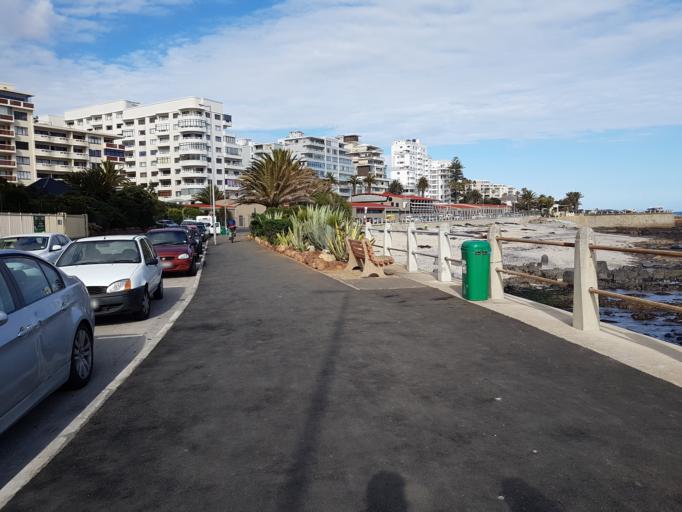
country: ZA
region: Western Cape
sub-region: City of Cape Town
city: Cape Town
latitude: -33.9193
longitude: 18.3818
